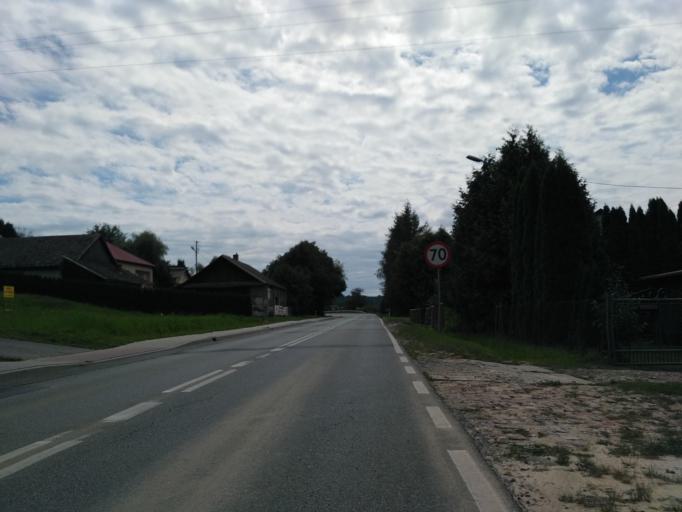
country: PL
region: Subcarpathian Voivodeship
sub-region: Powiat rzeszowski
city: Chmielnik
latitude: 49.9473
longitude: 22.1010
